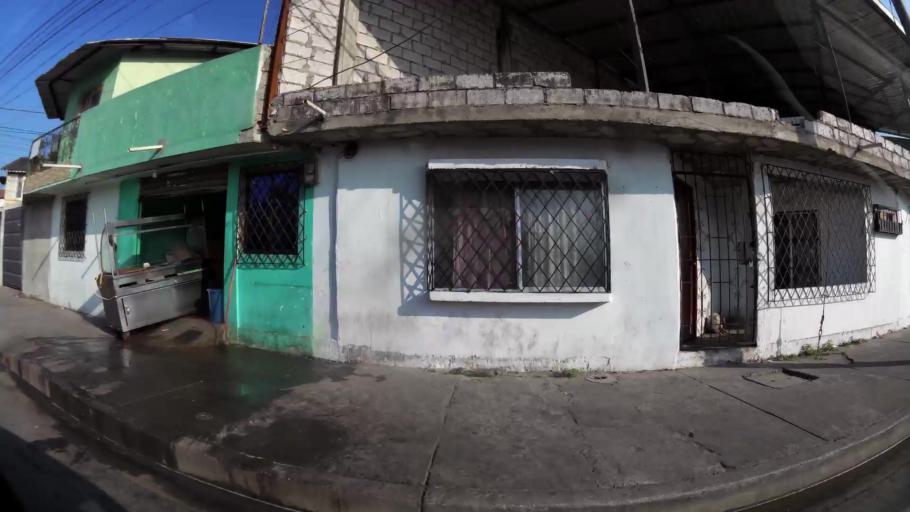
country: EC
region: Guayas
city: Eloy Alfaro
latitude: -2.1854
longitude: -79.8527
